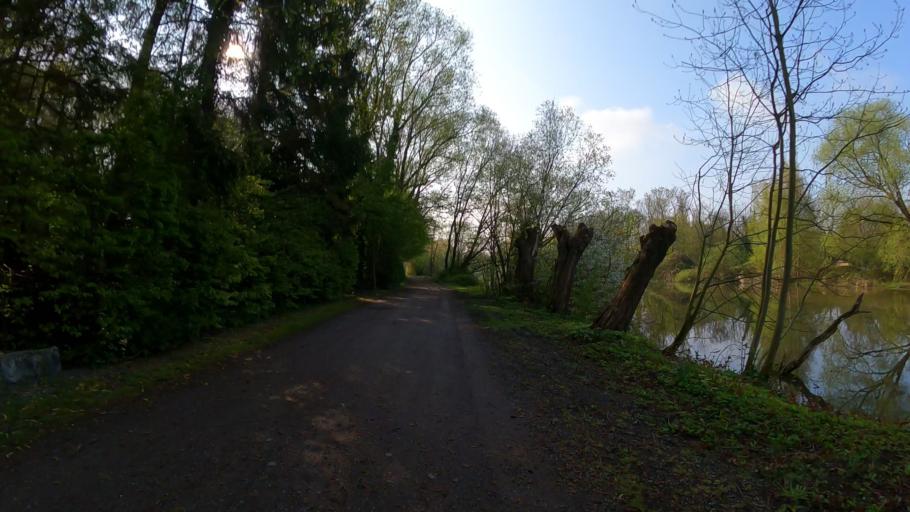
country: DE
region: Hamburg
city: Kleiner Grasbrook
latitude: 53.5066
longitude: 10.0160
